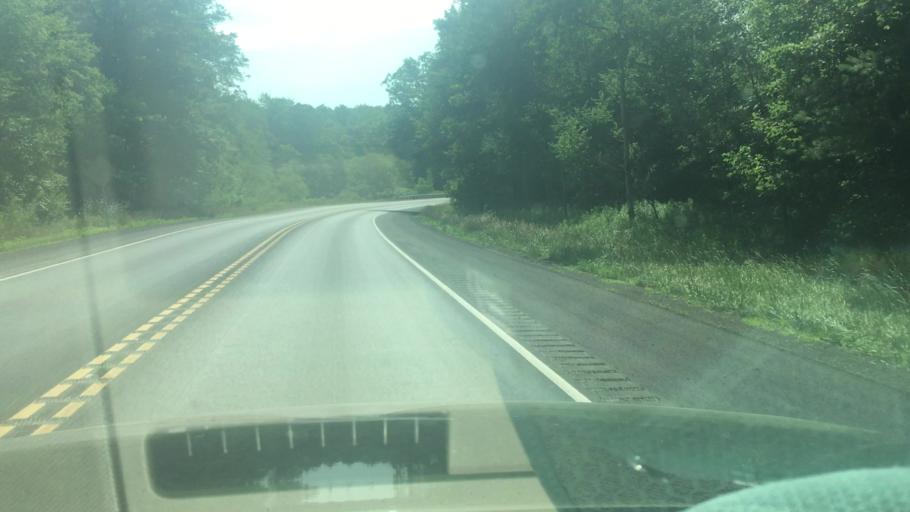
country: US
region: Pennsylvania
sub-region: Northumberland County
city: Mount Carmel
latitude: 40.7688
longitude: -76.4334
